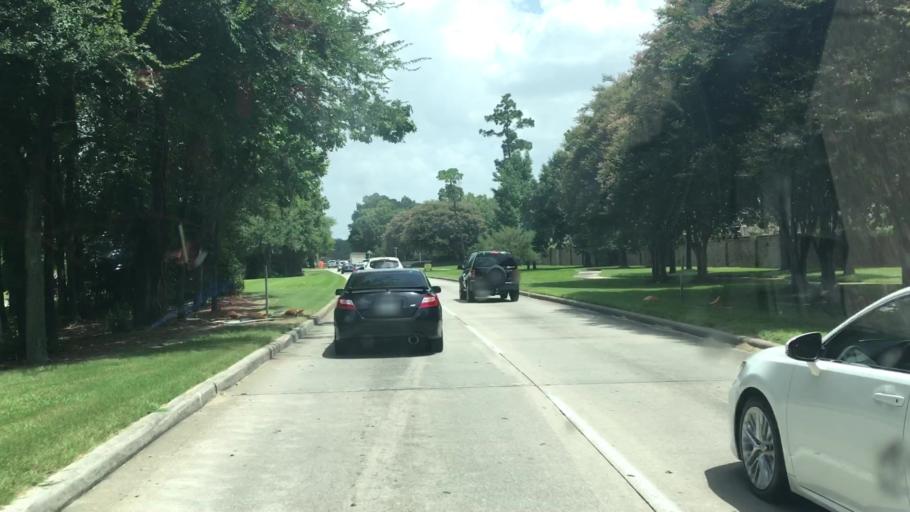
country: US
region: Texas
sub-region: Harris County
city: Atascocita
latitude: 29.9321
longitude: -95.1762
